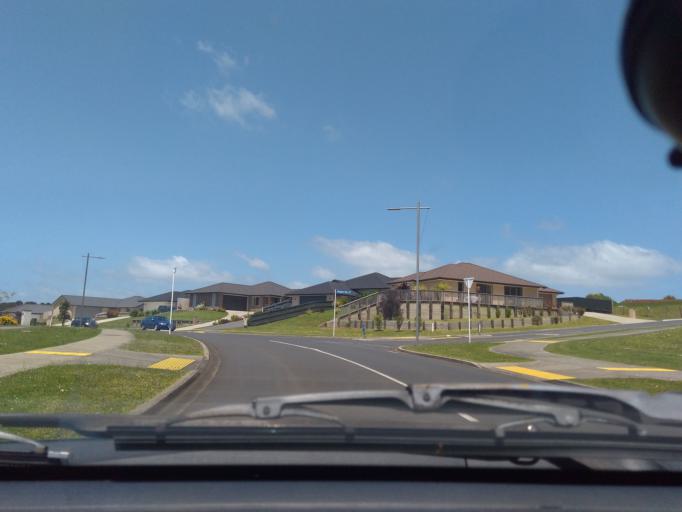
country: NZ
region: Northland
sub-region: Whangarei
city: Whangarei
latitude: -35.6756
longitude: 174.3158
